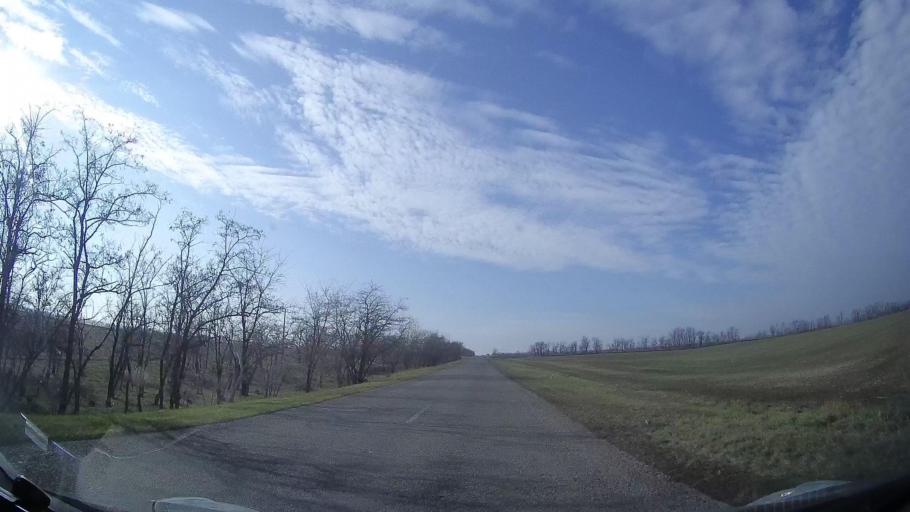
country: RU
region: Rostov
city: Gigant
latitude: 46.8492
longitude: 41.3098
